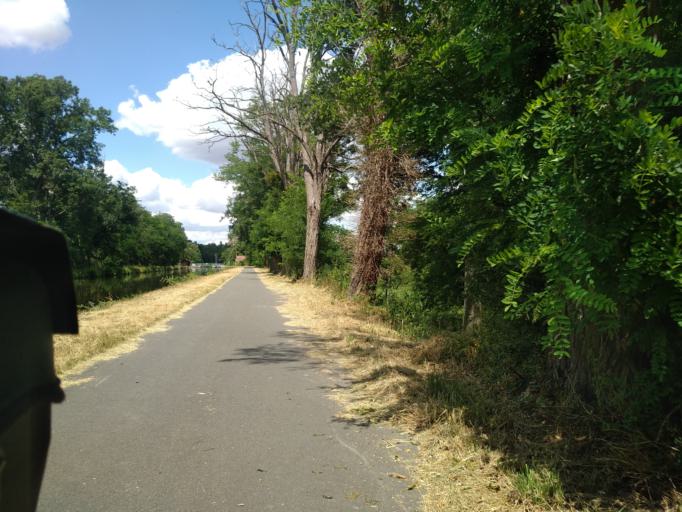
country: FR
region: Rhone-Alpes
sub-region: Departement de la Loire
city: Briennon
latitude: 46.1369
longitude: 4.0818
